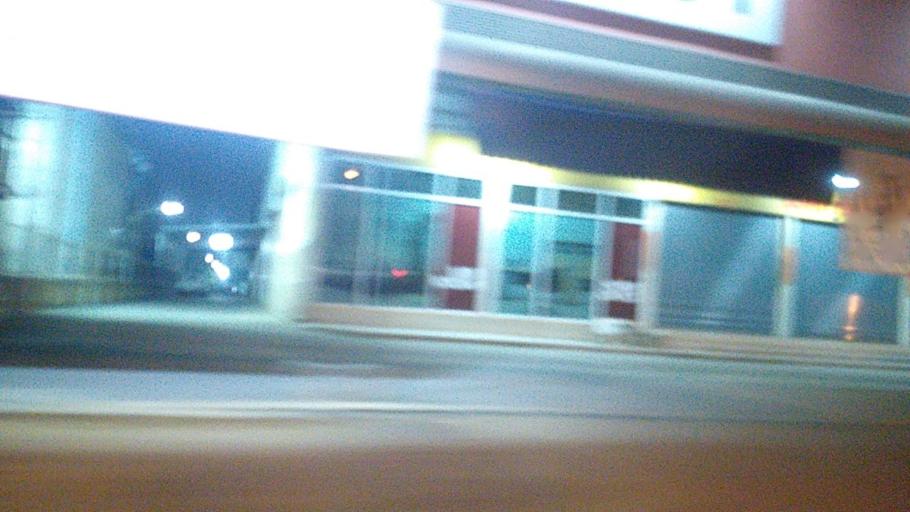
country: TH
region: Bangkok
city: Sai Mai
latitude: 13.9330
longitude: 100.6875
